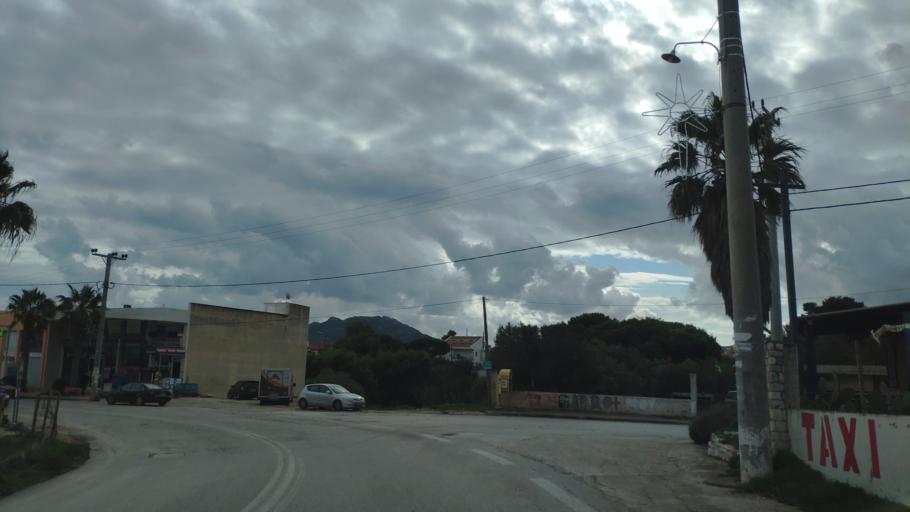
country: GR
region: Attica
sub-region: Nomarchia Anatolikis Attikis
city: Artemida
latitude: 37.9417
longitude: 24.0083
